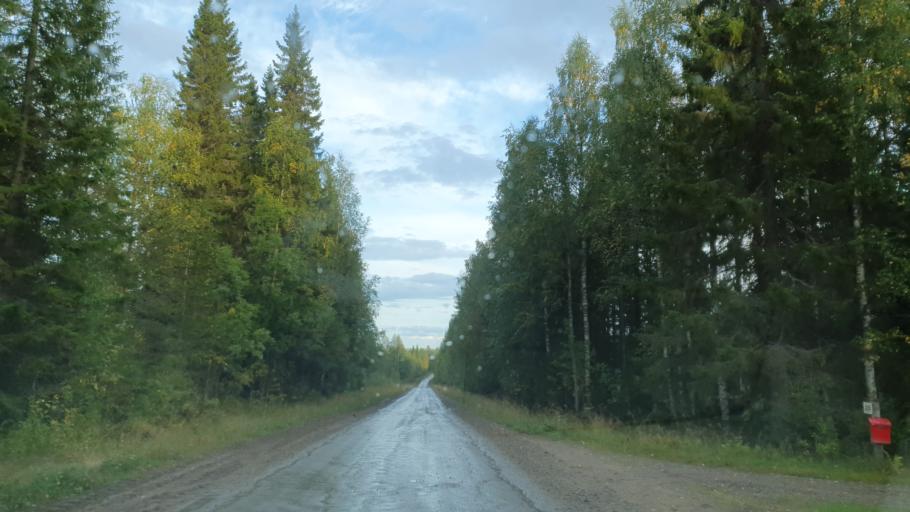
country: FI
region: Kainuu
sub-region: Kehys-Kainuu
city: Kuhmo
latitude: 64.3859
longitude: 29.4322
